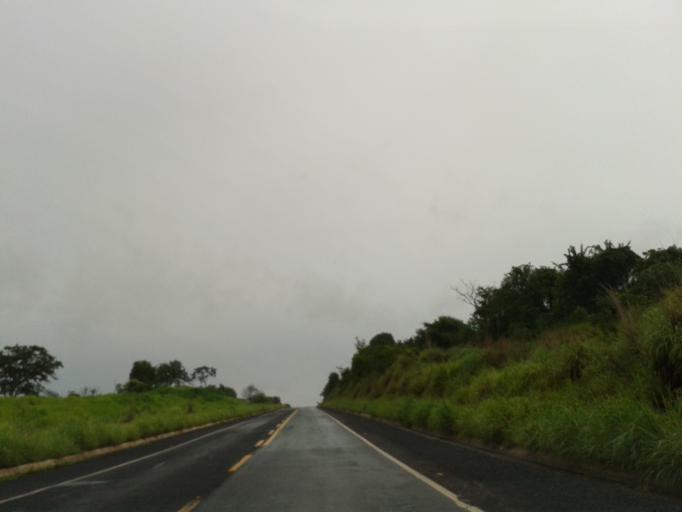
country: BR
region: Minas Gerais
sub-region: Santa Vitoria
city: Santa Vitoria
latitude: -19.1208
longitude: -50.2976
